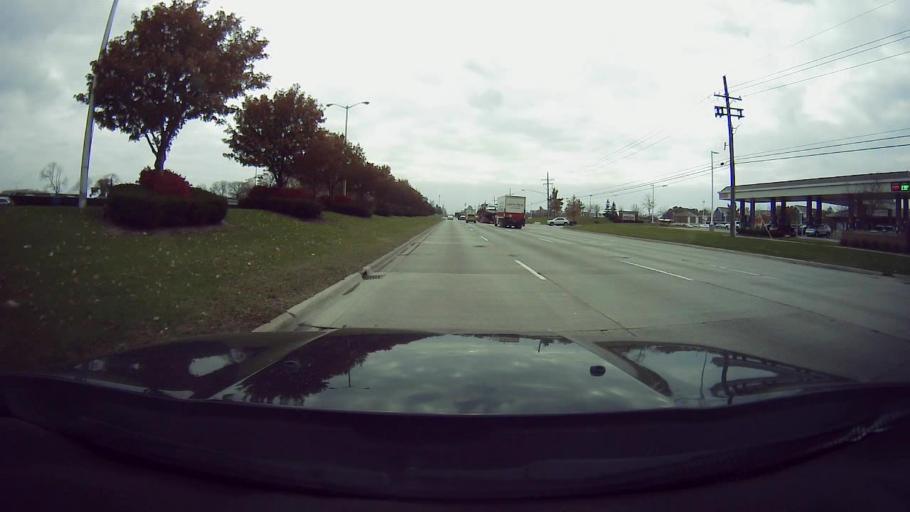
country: US
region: Michigan
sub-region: Macomb County
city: Center Line
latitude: 42.5117
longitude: -83.0469
